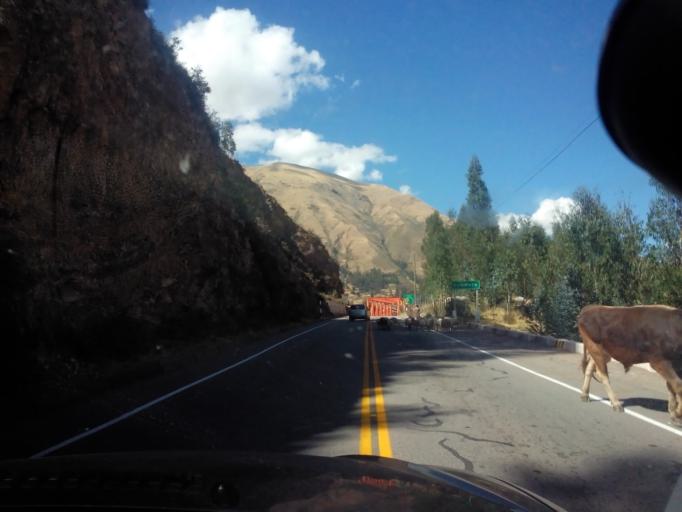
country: PE
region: Cusco
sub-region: Provincia de Quispicanchis
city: Cusipata
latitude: -13.8983
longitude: -71.5013
